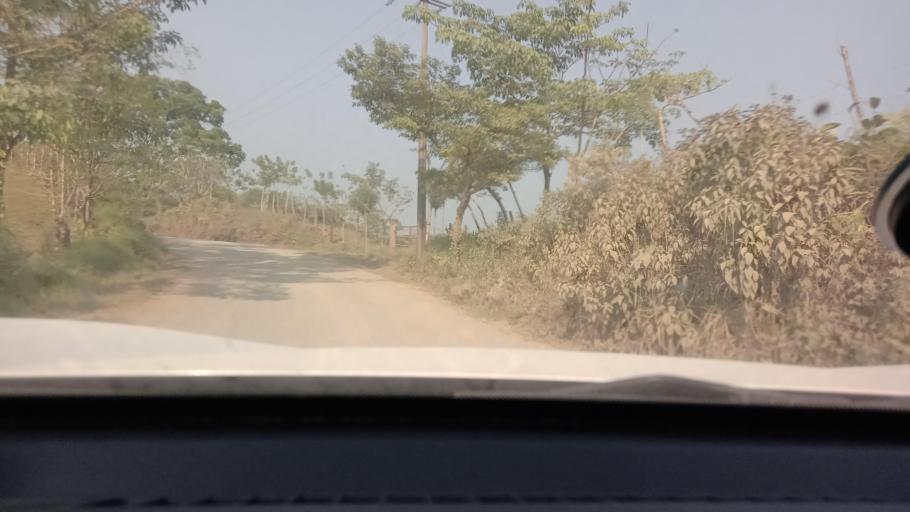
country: MX
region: Tabasco
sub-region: Huimanguillo
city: Francisco Rueda
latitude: 17.6538
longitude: -93.8939
